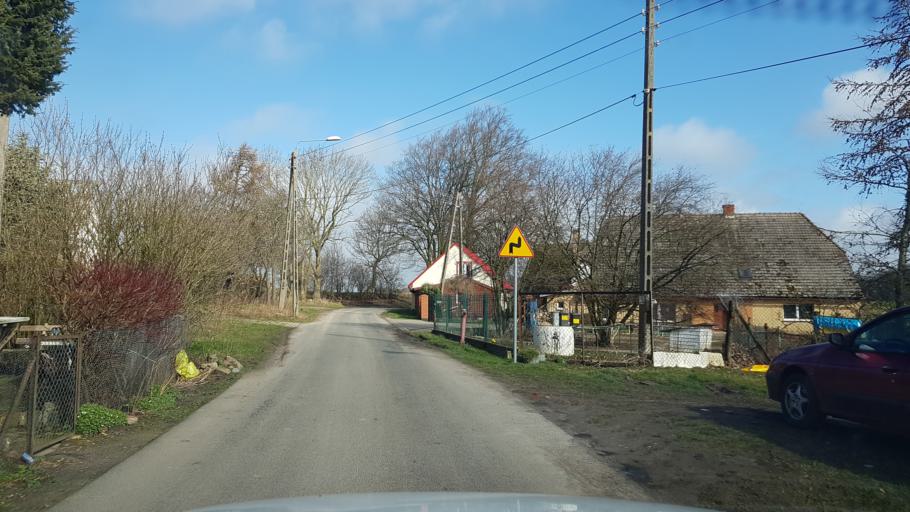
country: PL
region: West Pomeranian Voivodeship
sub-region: Powiat slawienski
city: Slawno
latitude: 54.4807
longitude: 16.6508
